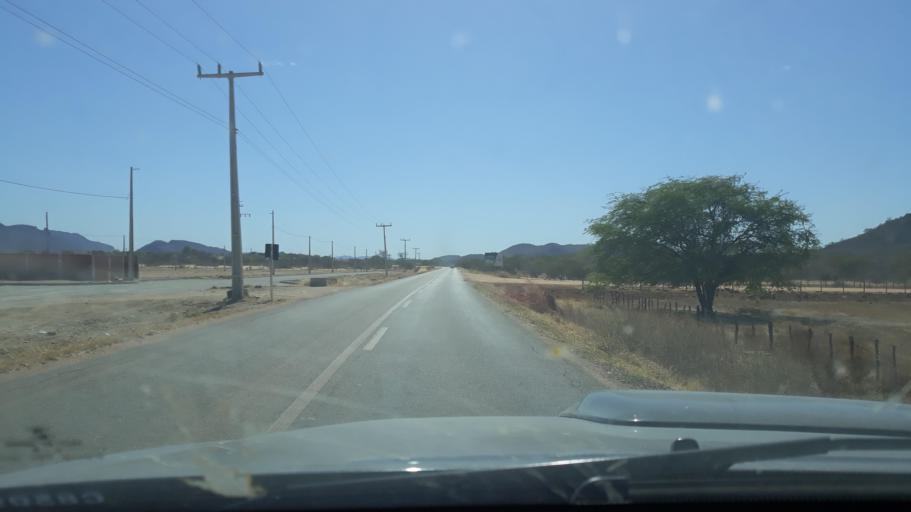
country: BR
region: Bahia
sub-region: Guanambi
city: Guanambi
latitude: -14.1865
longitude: -42.7986
